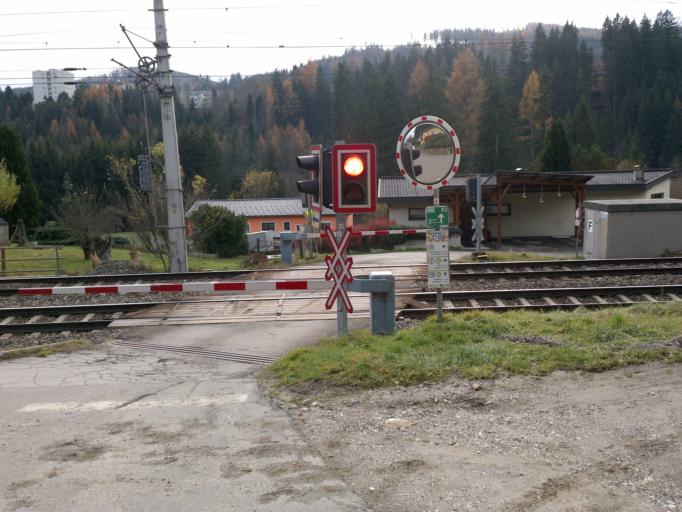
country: AT
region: Styria
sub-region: Politischer Bezirk Murtal
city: Judenburg
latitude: 47.1748
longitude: 14.6499
